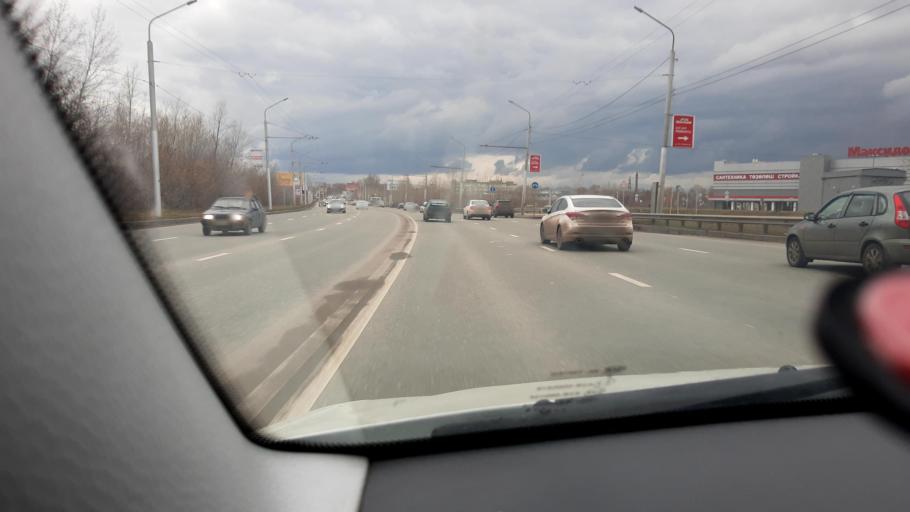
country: RU
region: Bashkortostan
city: Ufa
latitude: 54.7882
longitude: 56.0780
